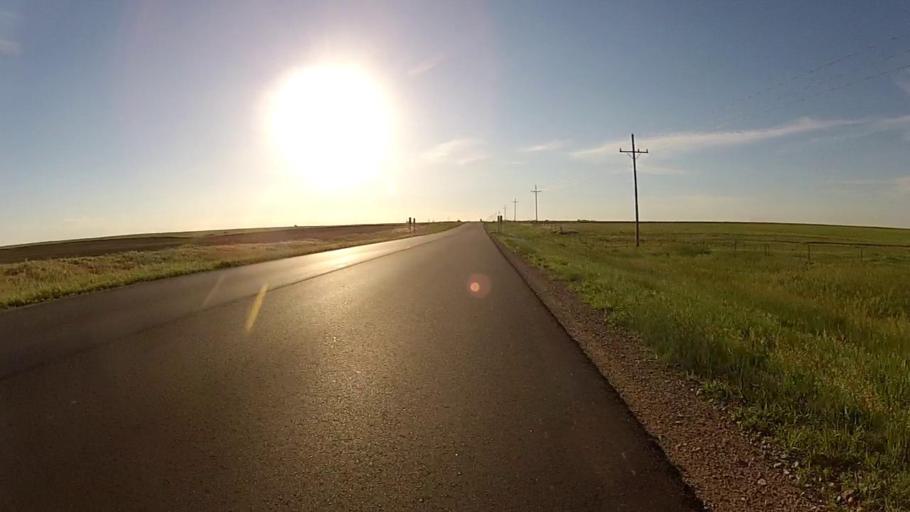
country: US
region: Kansas
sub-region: Comanche County
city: Coldwater
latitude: 37.2815
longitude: -99.1856
